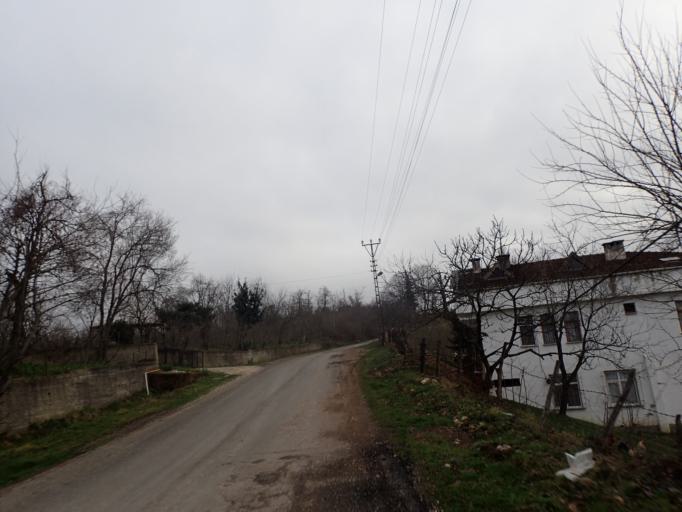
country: TR
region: Ordu
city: Camas
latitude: 40.9285
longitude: 37.5186
